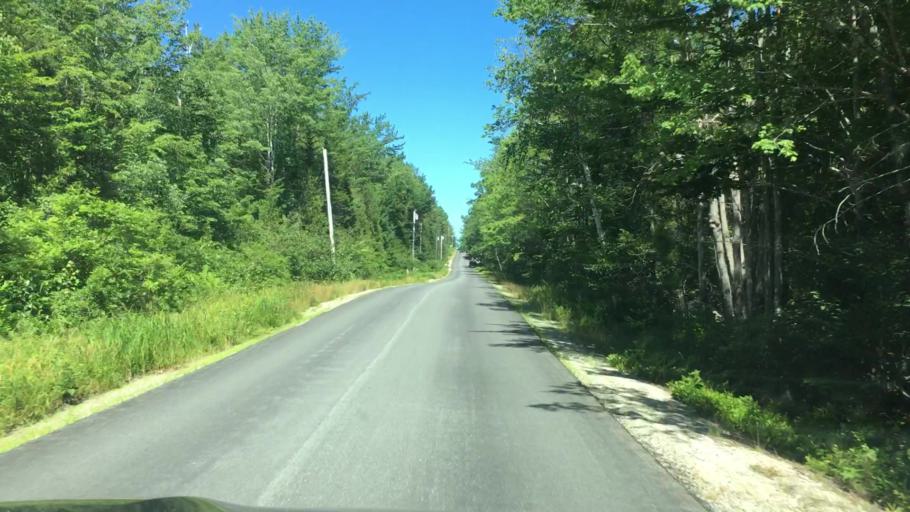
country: US
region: Maine
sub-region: Hancock County
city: Sedgwick
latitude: 44.3170
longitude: -68.6220
